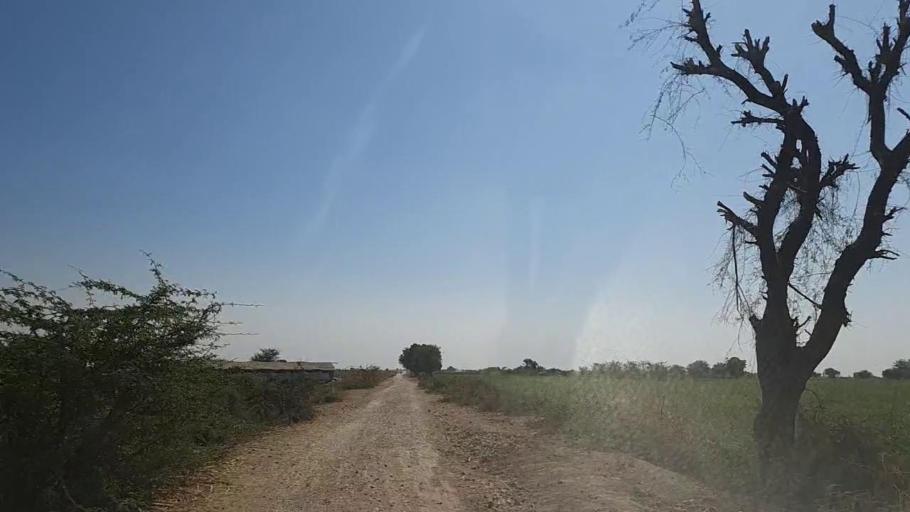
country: PK
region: Sindh
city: Kunri
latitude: 25.2783
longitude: 69.5226
